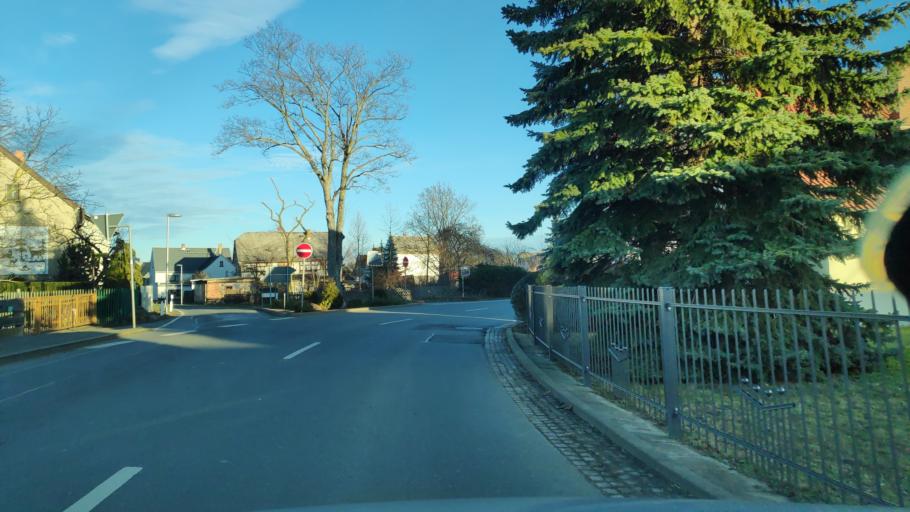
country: DE
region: Thuringia
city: Jonaswalde
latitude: 50.8053
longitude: 12.3082
